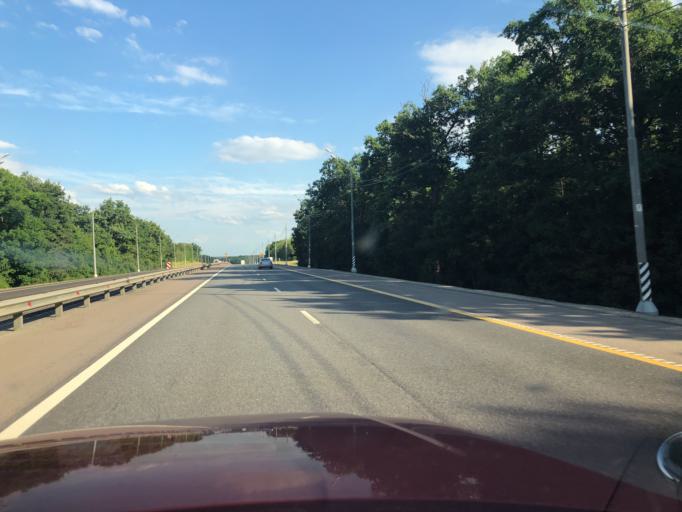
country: RU
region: Lipetsk
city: Zadonsk
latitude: 52.4153
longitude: 38.8430
